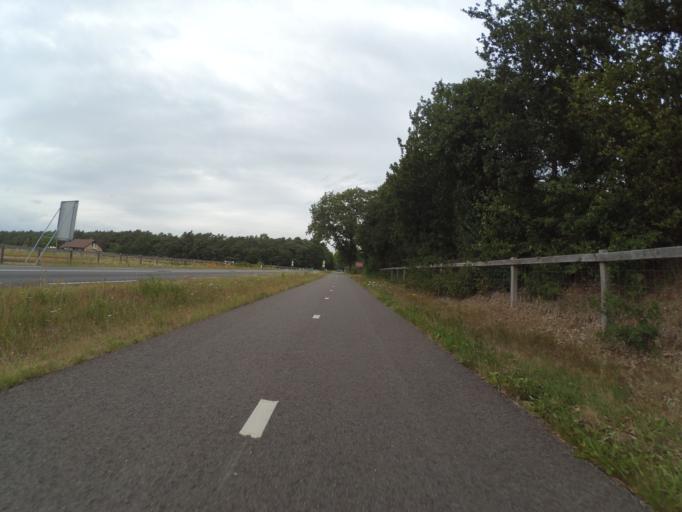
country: NL
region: Gelderland
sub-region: Gemeente Ede
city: Otterlo
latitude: 52.0884
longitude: 5.7763
